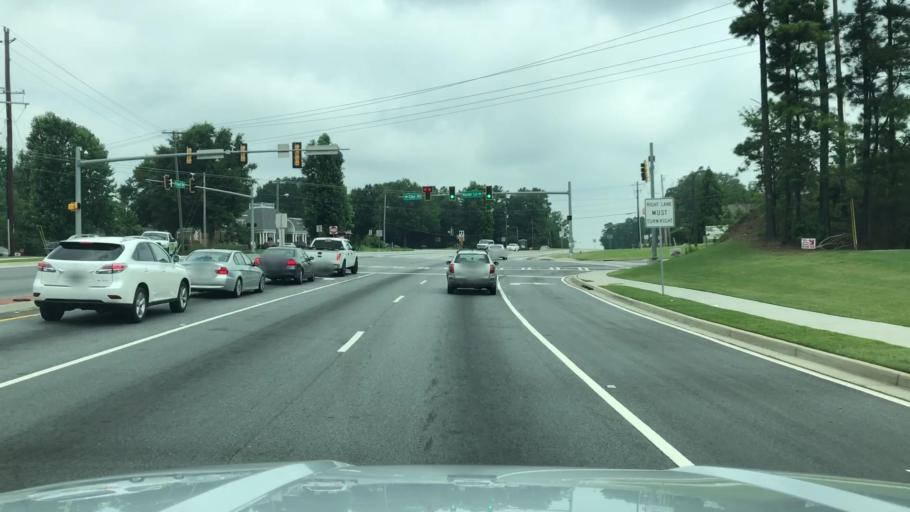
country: US
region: Georgia
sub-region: Cobb County
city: Mableton
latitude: 33.8246
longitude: -84.5758
